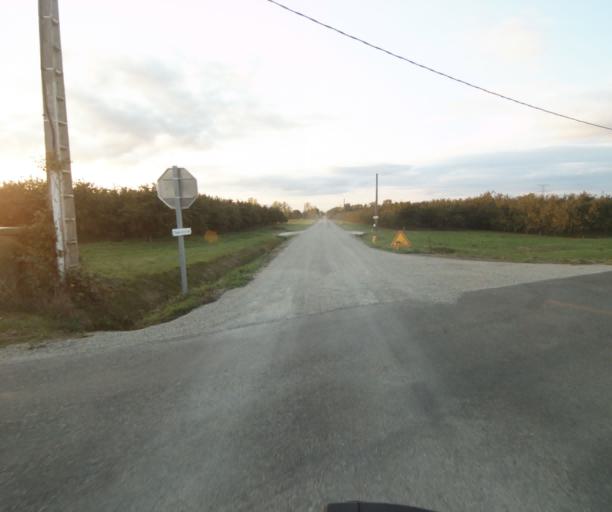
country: FR
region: Midi-Pyrenees
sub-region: Departement du Tarn-et-Garonne
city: Verdun-sur-Garonne
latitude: 43.8310
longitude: 1.2266
